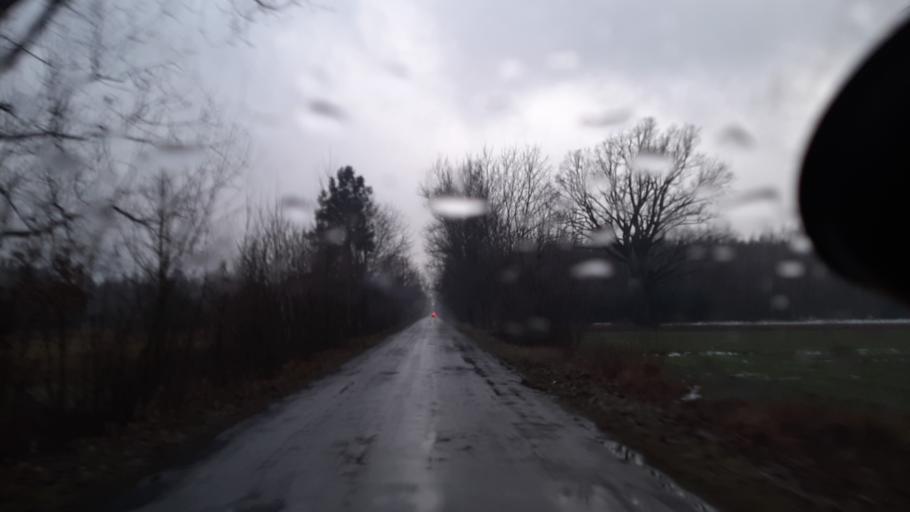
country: PL
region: Lublin Voivodeship
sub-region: Powiat lubartowski
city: Firlej
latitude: 51.5234
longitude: 22.4993
